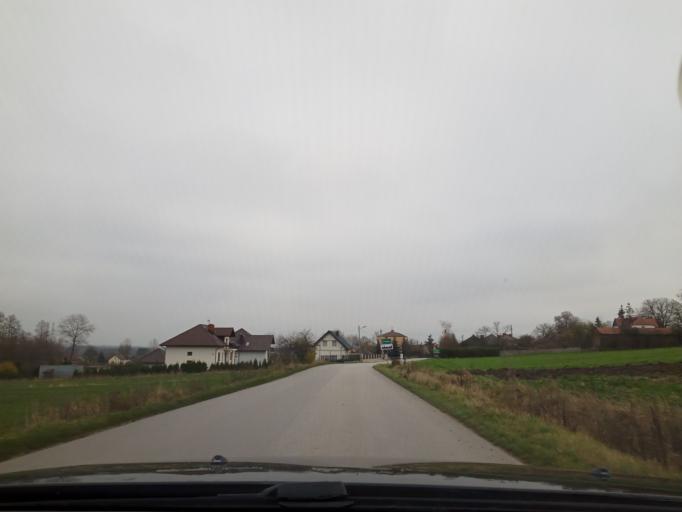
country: PL
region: Swietokrzyskie
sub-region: Powiat jedrzejowski
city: Imielno
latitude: 50.5875
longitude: 20.4424
